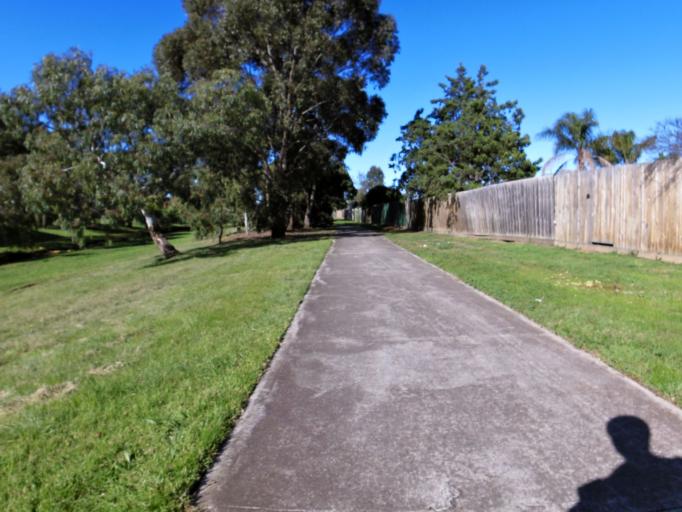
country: AU
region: Victoria
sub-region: Wyndham
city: Tarneit
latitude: -37.8771
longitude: 144.6749
